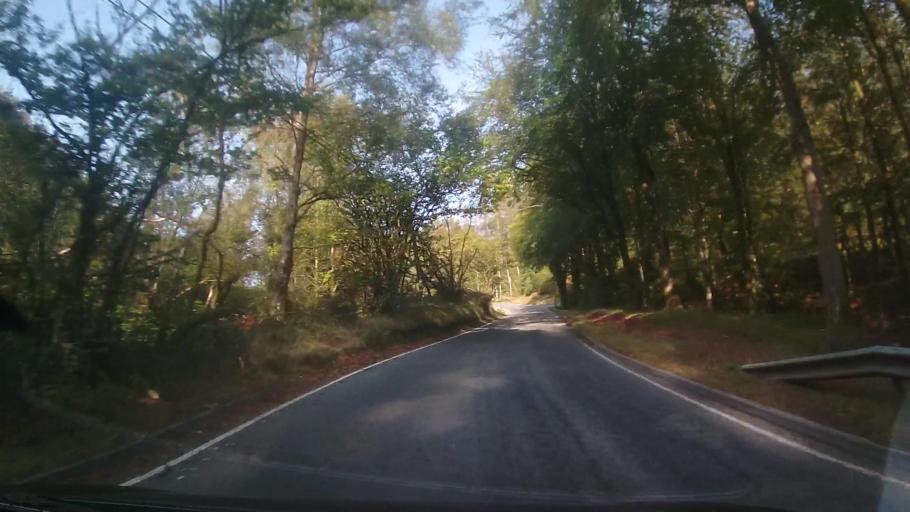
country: GB
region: Wales
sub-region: County of Ceredigion
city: Lledrod
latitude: 52.3425
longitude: -3.8372
